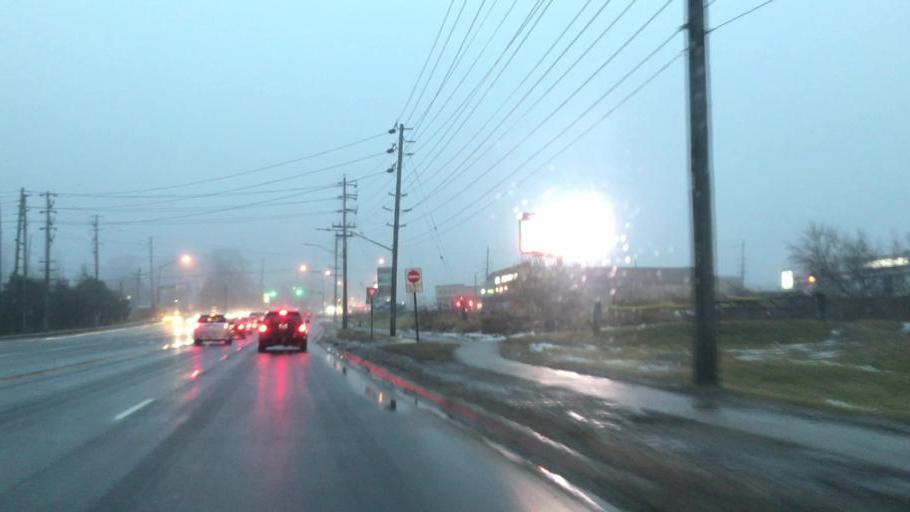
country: CA
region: Ontario
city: Newmarket
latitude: 44.0405
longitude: -79.4566
